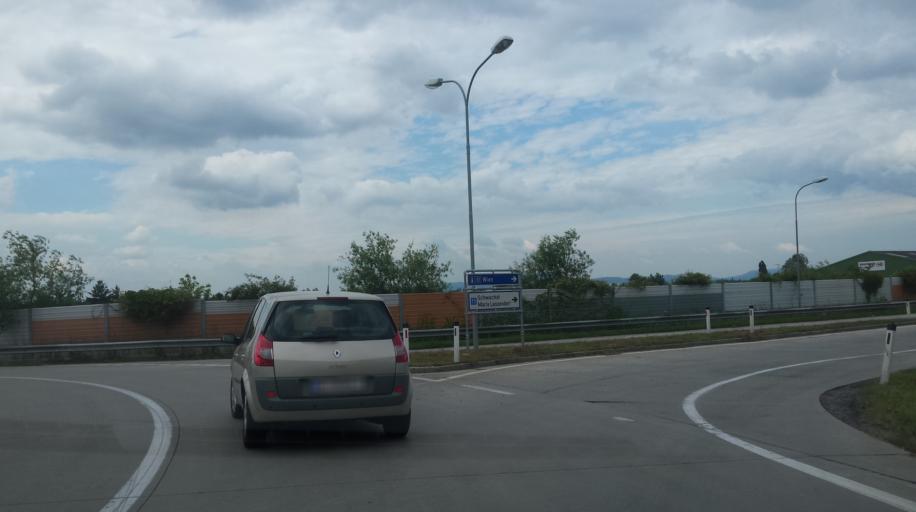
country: AT
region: Lower Austria
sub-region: Politischer Bezirk Wien-Umgebung
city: Himberg
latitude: 48.0925
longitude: 16.4469
